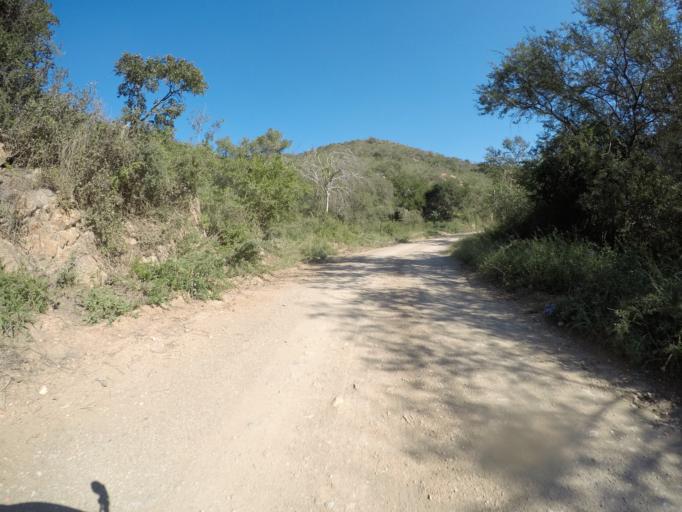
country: ZA
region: Eastern Cape
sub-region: Cacadu District Municipality
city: Kareedouw
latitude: -33.6595
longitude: 24.5270
